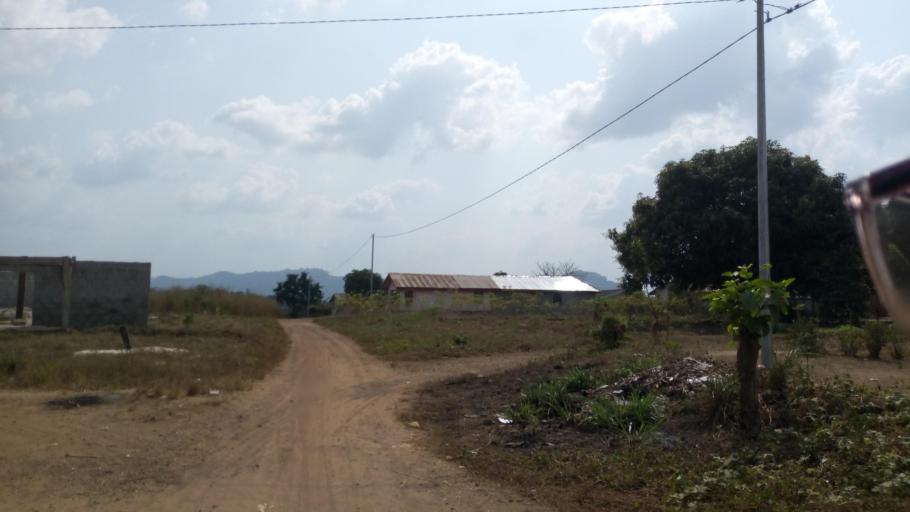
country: SL
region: Southern Province
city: Mogbwemo
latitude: 7.7746
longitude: -12.3000
